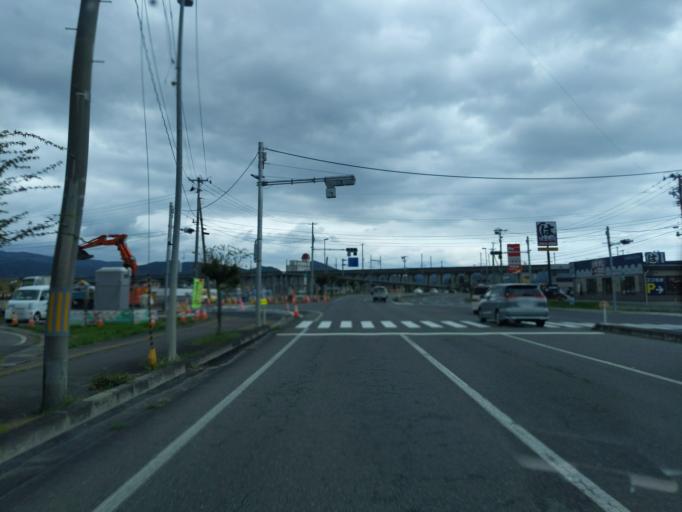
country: JP
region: Iwate
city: Ichinoseki
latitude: 38.9403
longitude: 141.1413
